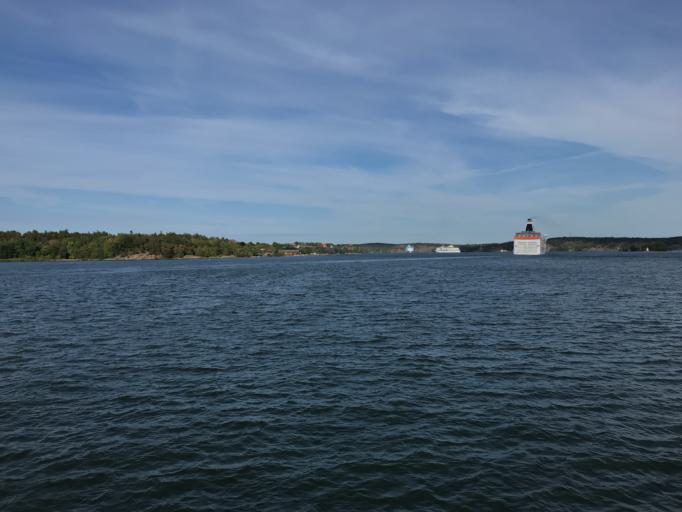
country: SE
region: Stockholm
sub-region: Nacka Kommun
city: Nacka
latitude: 59.3369
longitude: 18.1533
